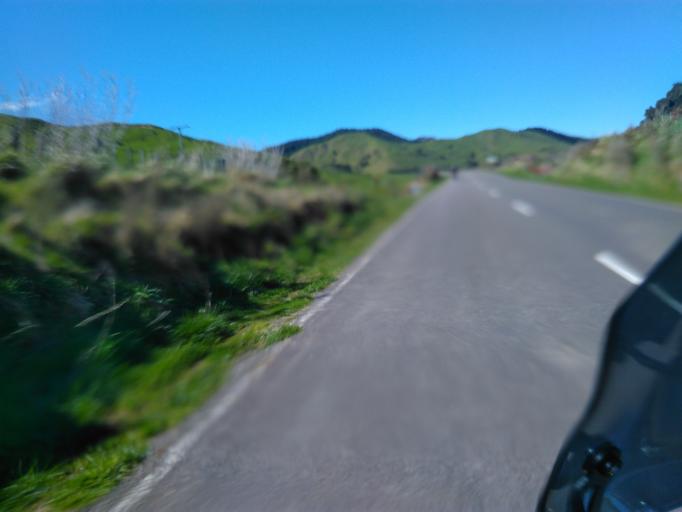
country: NZ
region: Bay of Plenty
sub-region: Opotiki District
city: Opotiki
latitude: -38.3107
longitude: 177.5237
